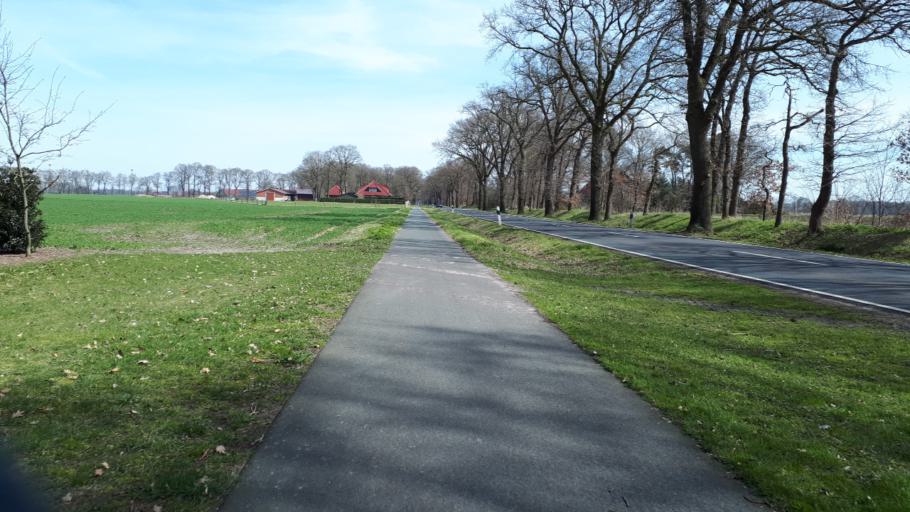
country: DE
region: Lower Saxony
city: Garrel
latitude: 52.9774
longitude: 8.0701
